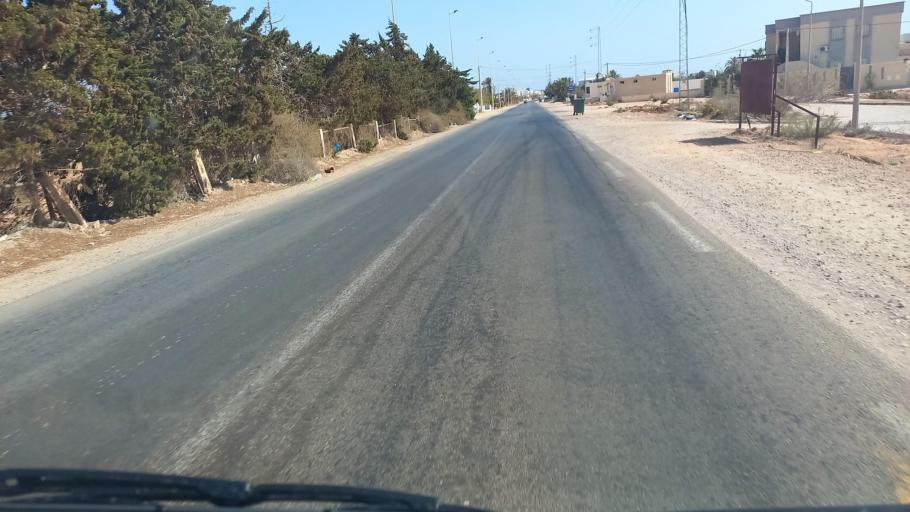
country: TN
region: Madanin
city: Midoun
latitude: 33.7720
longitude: 11.0261
